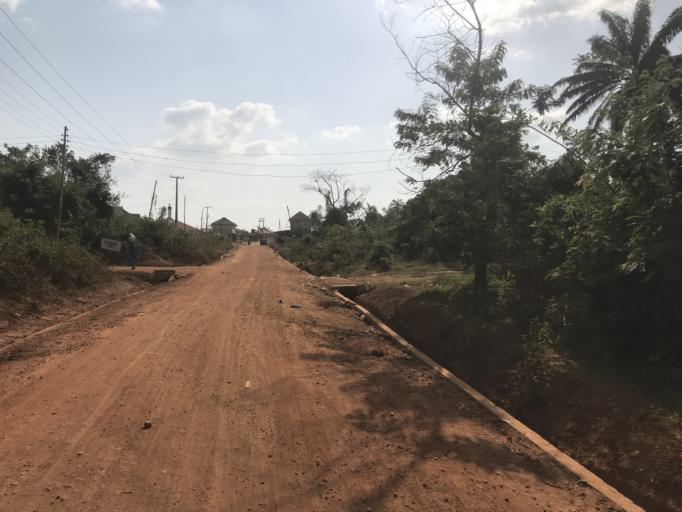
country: NG
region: Osun
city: Osogbo
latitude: 7.8186
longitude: 4.5636
